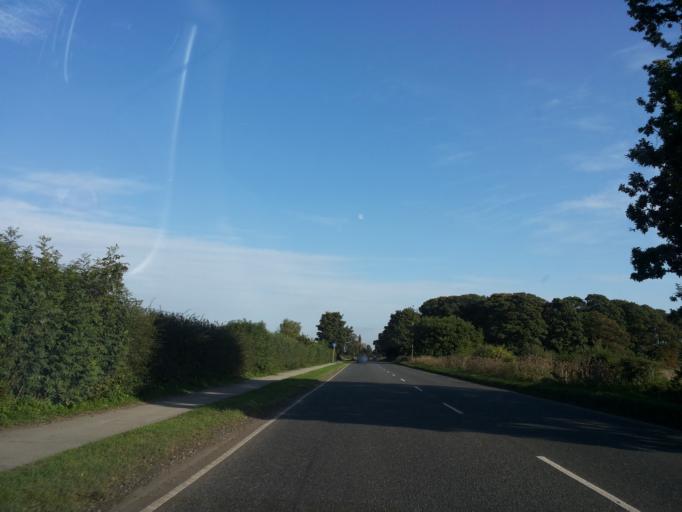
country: GB
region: England
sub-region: East Riding of Yorkshire
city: Snaith
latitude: 53.6875
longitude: -1.0088
